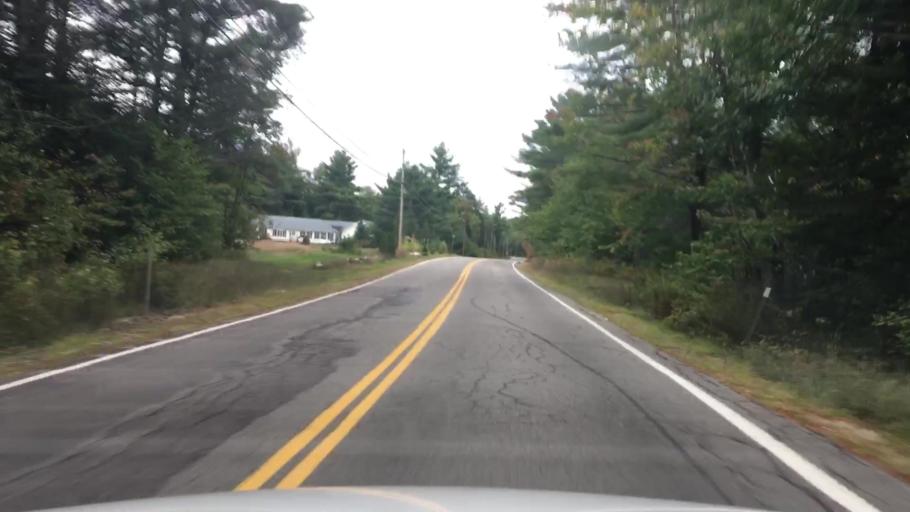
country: US
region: New Hampshire
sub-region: Carroll County
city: Effingham
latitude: 43.7454
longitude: -71.0044
